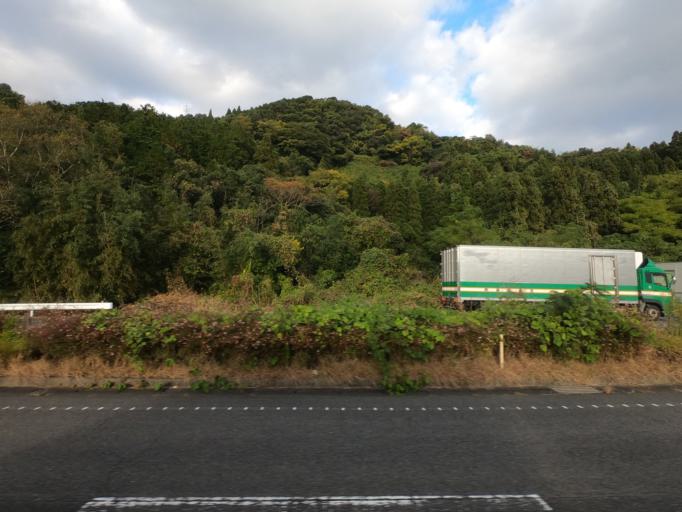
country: JP
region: Kumamoto
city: Minamata
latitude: 32.2413
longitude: 130.4816
